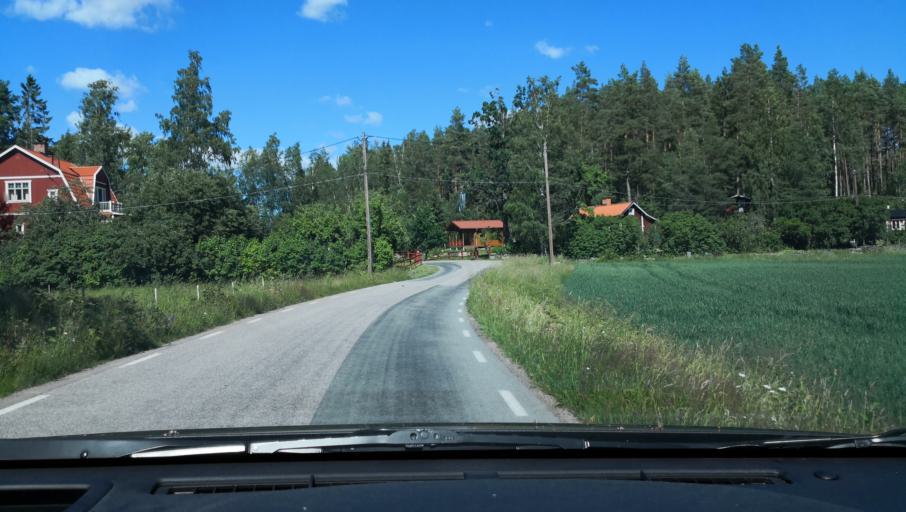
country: SE
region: Soedermanland
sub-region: Eskilstuna Kommun
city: Hallbybrunn
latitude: 59.3123
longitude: 16.3763
